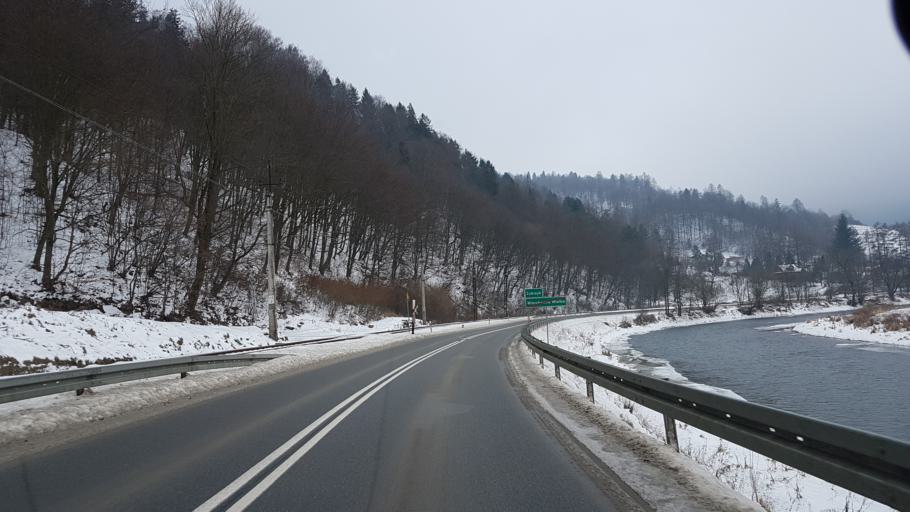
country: PL
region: Lesser Poland Voivodeship
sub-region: Powiat nowosadecki
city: Piwniczna-Zdroj
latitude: 49.4001
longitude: 20.7588
